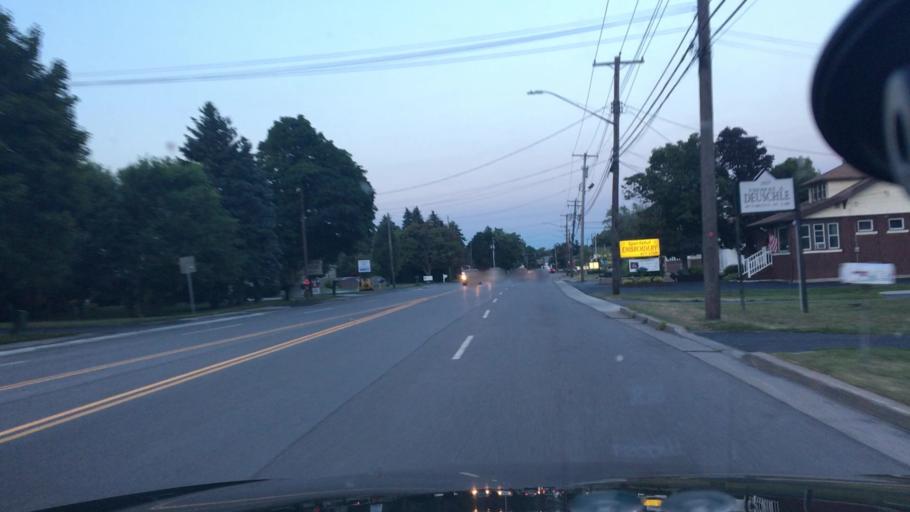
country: US
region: New York
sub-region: Erie County
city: West Seneca
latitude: 42.8295
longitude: -78.7717
